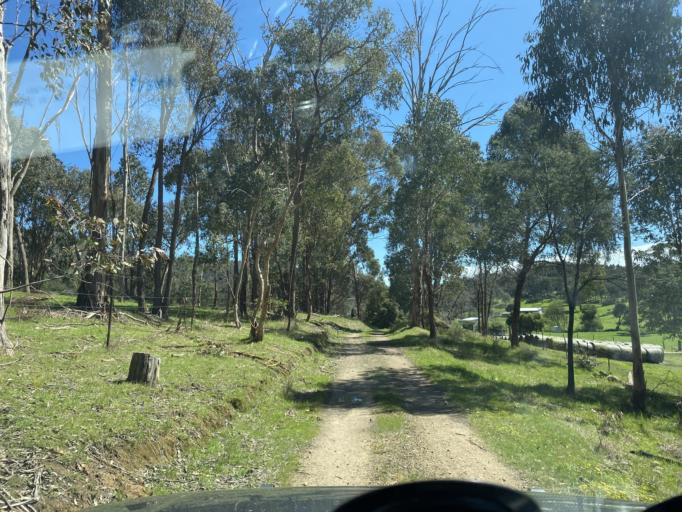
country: AU
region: Victoria
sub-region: Benalla
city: Benalla
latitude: -36.7128
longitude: 146.1822
